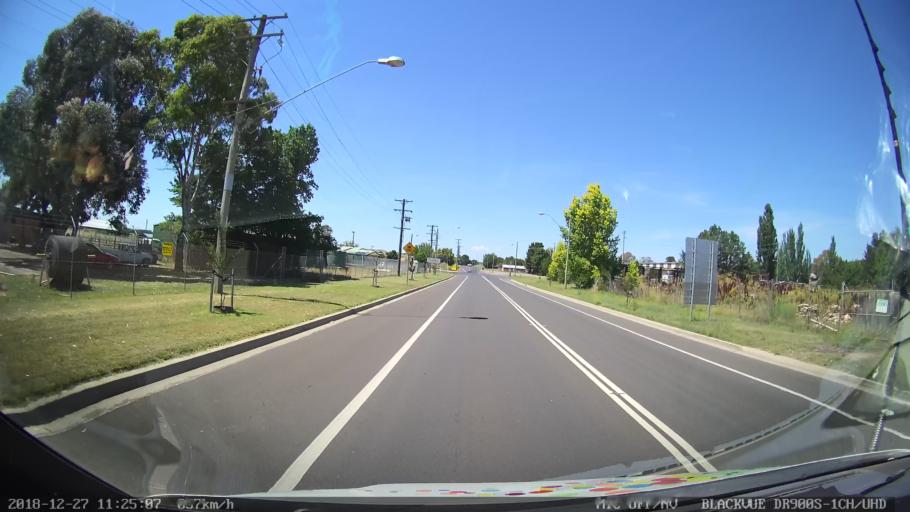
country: AU
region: New South Wales
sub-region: Bathurst Regional
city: Bathurst
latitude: -33.4391
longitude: 149.5786
